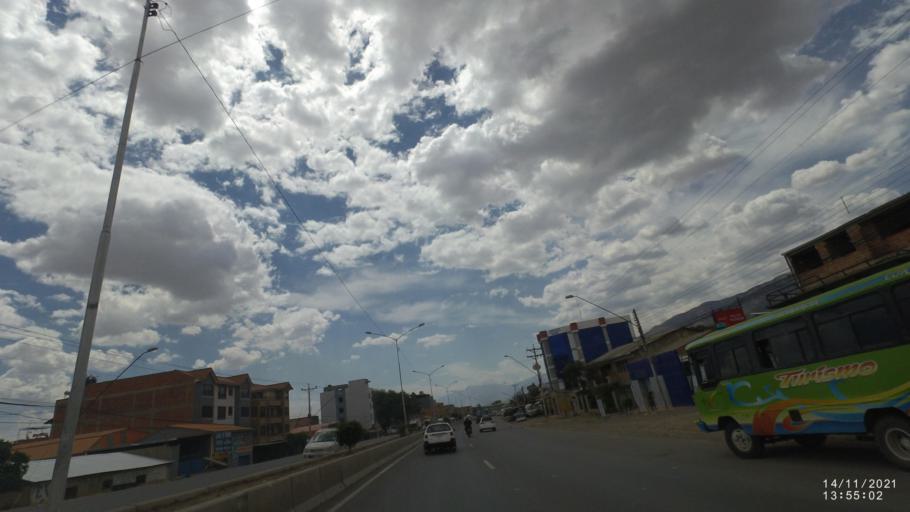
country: BO
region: Cochabamba
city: Cochabamba
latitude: -17.4024
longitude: -66.0327
